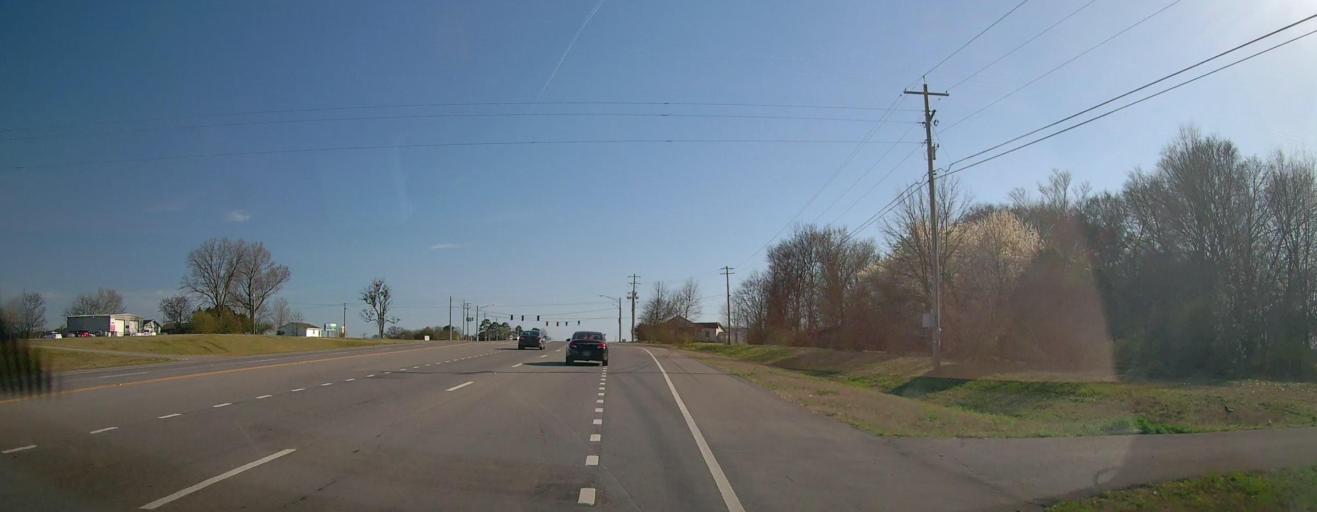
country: US
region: Alabama
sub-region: Colbert County
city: Muscle Shoals
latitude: 34.7026
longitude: -87.6348
